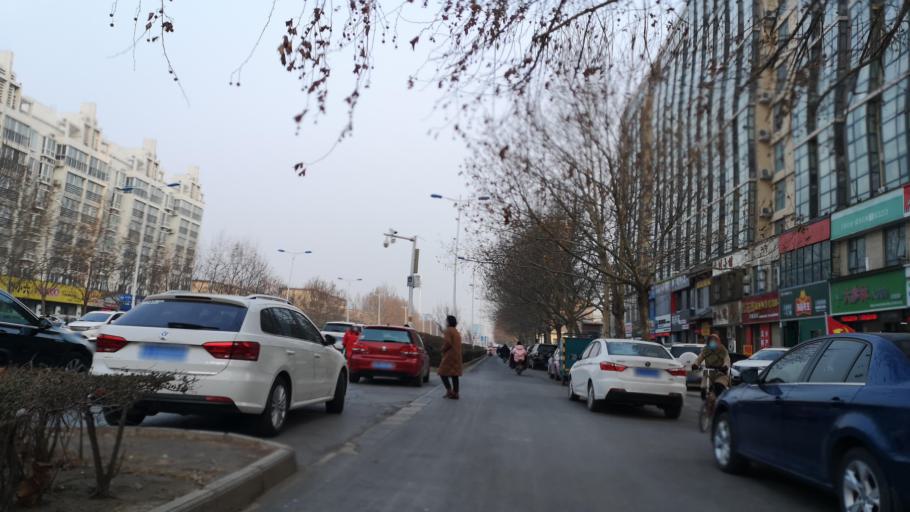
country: CN
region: Henan Sheng
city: Zhongyuanlu
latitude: 35.7653
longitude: 115.0924
